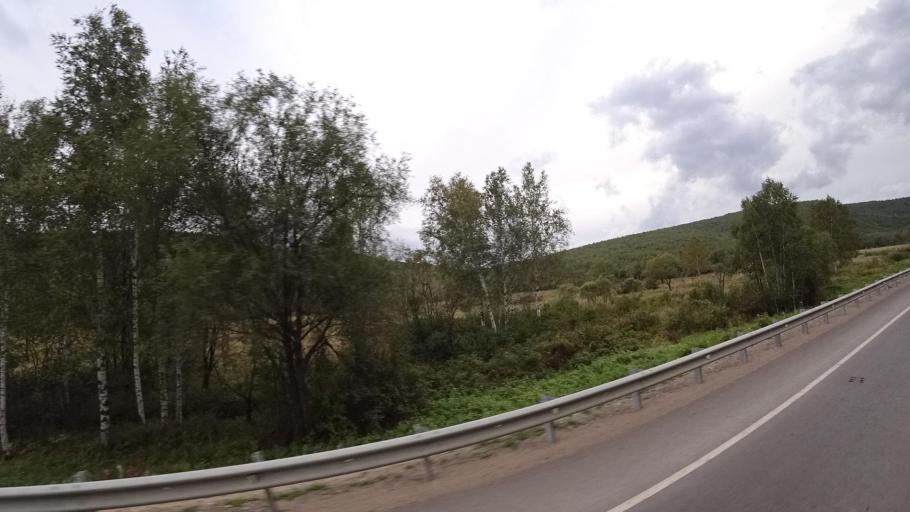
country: RU
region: Jewish Autonomous Oblast
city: Khingansk
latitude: 48.9832
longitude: 131.1502
